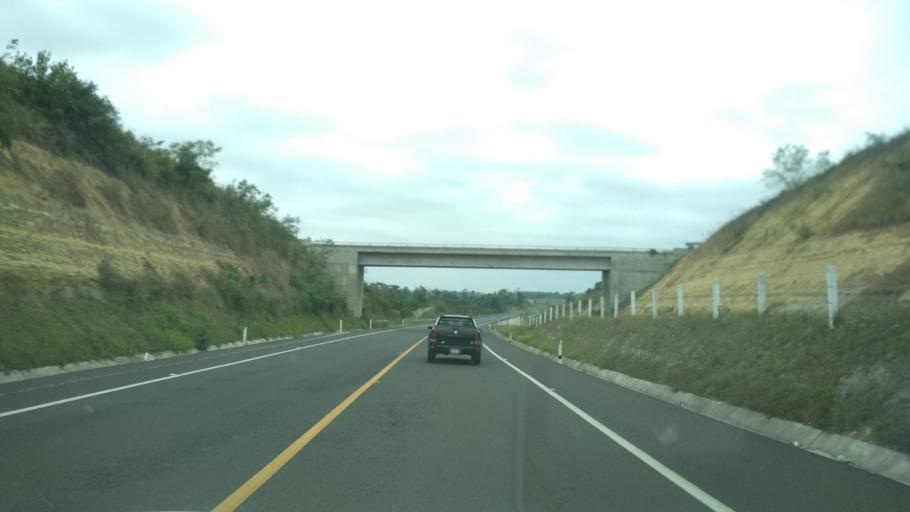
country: MX
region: Veracruz
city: Agua Dulce
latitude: 20.4344
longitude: -97.2308
